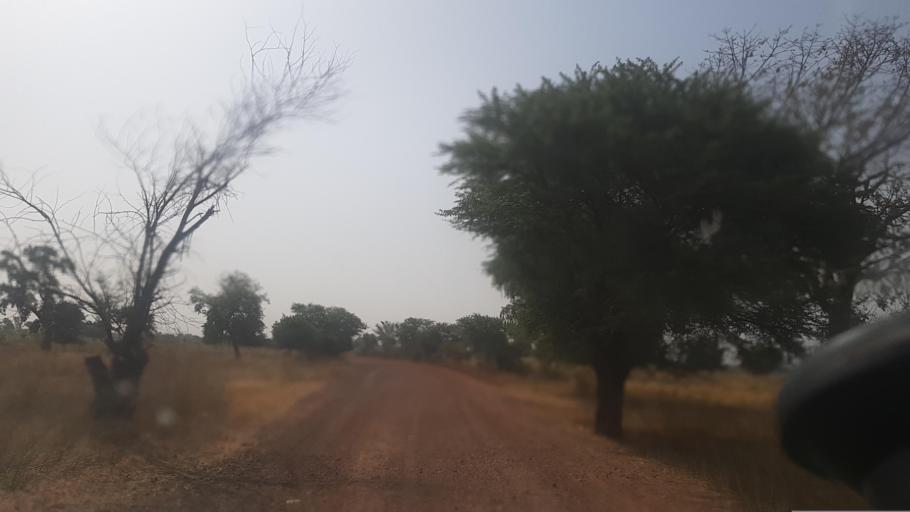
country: ML
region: Segou
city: Baroueli
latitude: 13.1460
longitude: -6.5158
